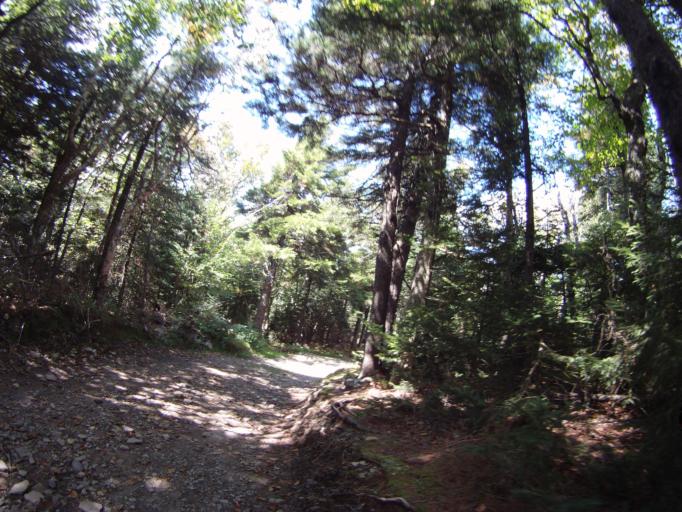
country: US
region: New York
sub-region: Ulster County
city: Woodstock
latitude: 42.1885
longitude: -74.2370
